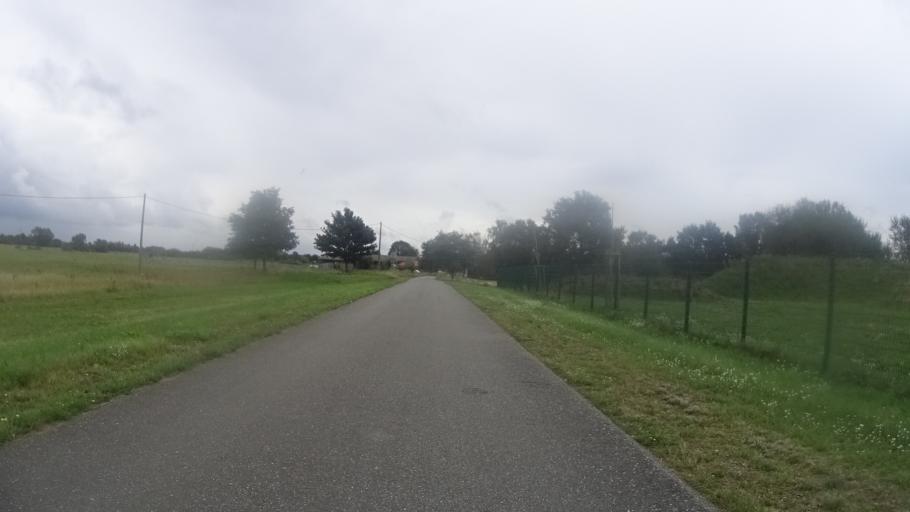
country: DE
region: Lower Saxony
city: Bleckede
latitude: 53.2926
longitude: 10.7957
